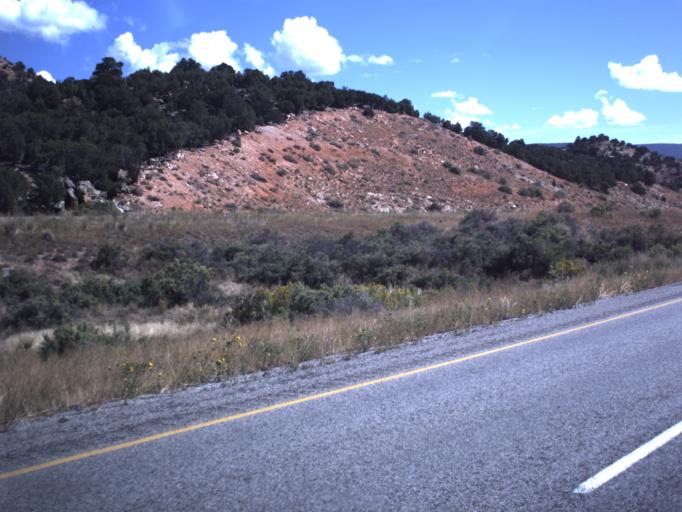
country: US
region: Utah
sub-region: Sevier County
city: Salina
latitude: 38.9220
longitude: -111.7652
